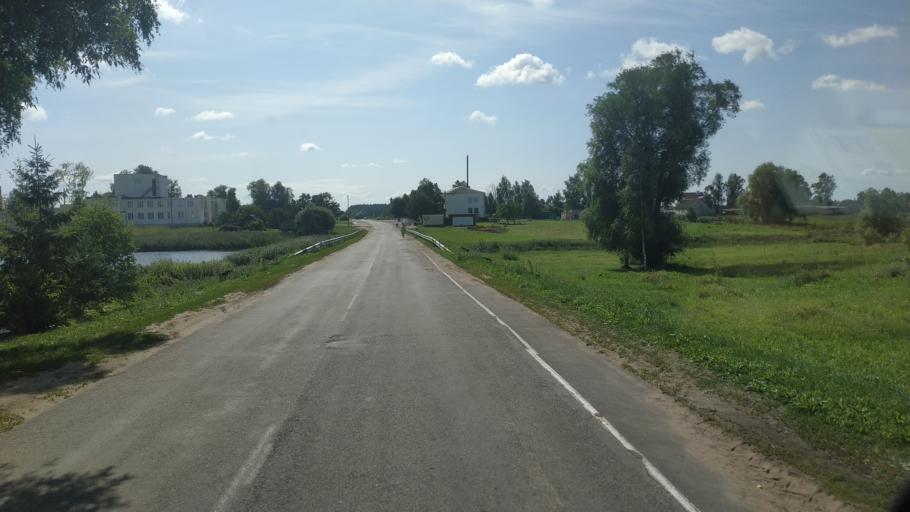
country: BY
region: Mogilev
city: Ramanavichy
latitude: 53.7054
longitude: 30.5040
